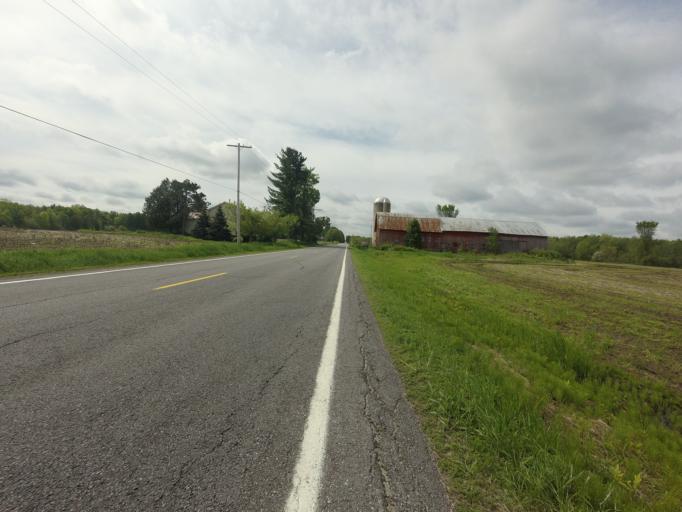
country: CA
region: Ontario
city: Cornwall
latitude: 44.7493
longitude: -74.6680
